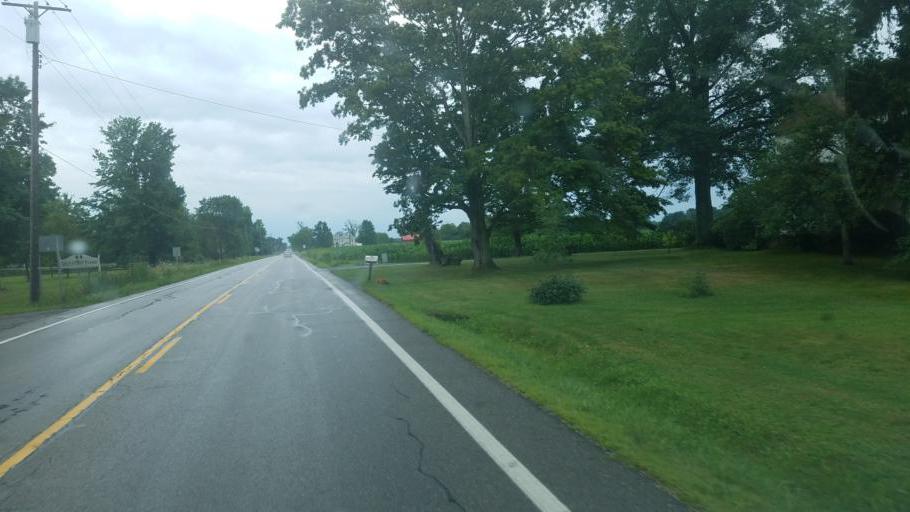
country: US
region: Ohio
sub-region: Ashtabula County
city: Orwell
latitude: 41.4570
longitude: -80.8686
